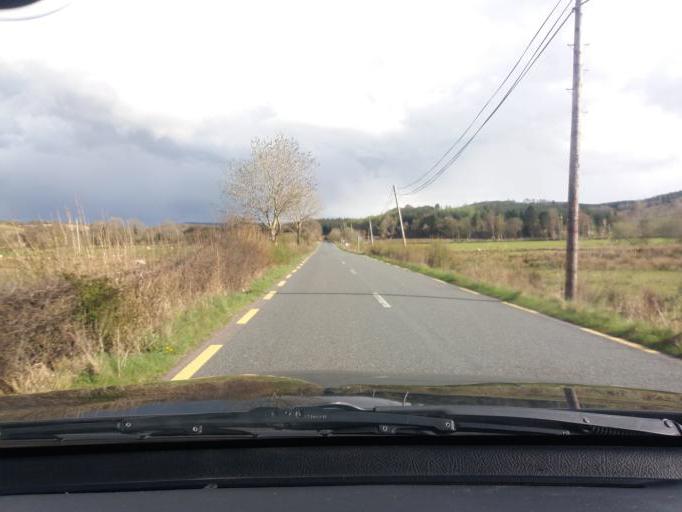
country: IE
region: Connaught
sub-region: County Leitrim
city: Manorhamilton
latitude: 54.3359
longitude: -8.2202
